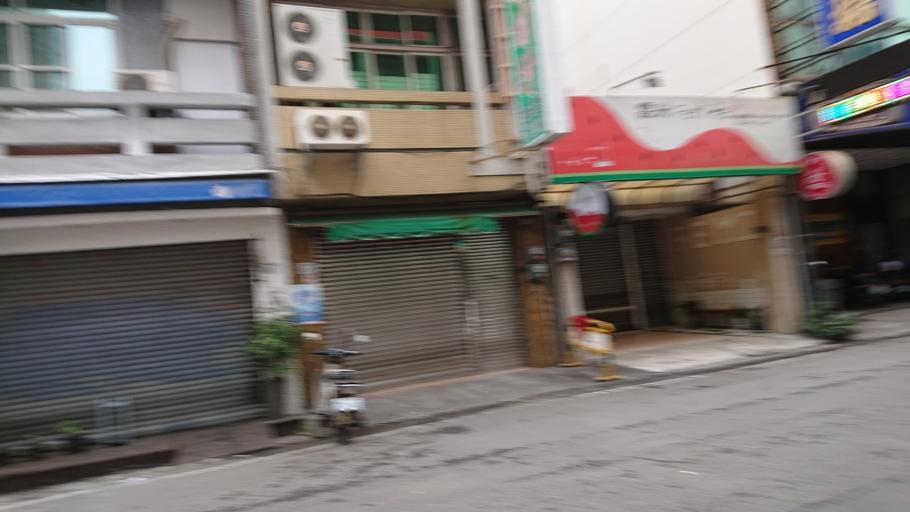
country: TW
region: Taiwan
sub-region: Chiayi
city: Jiayi Shi
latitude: 23.4819
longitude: 120.4467
